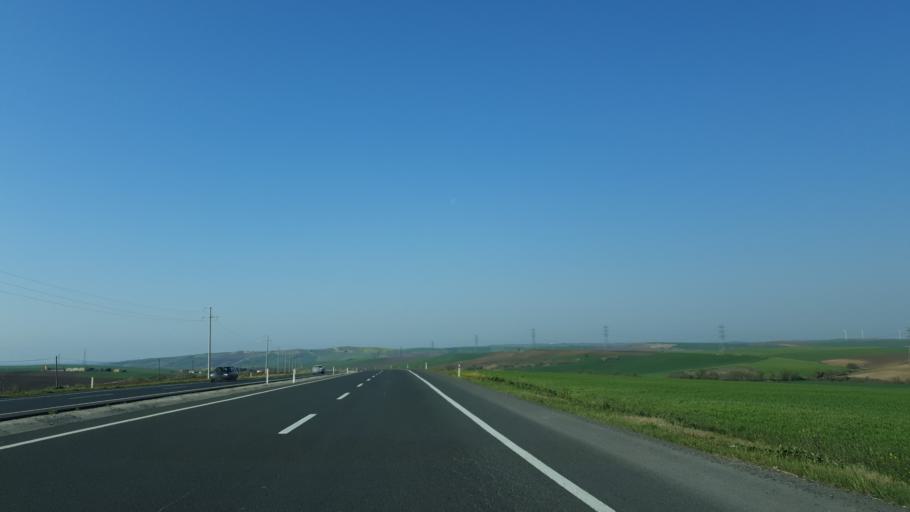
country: TR
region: Tekirdag
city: Corlu
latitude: 41.0969
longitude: 27.7518
